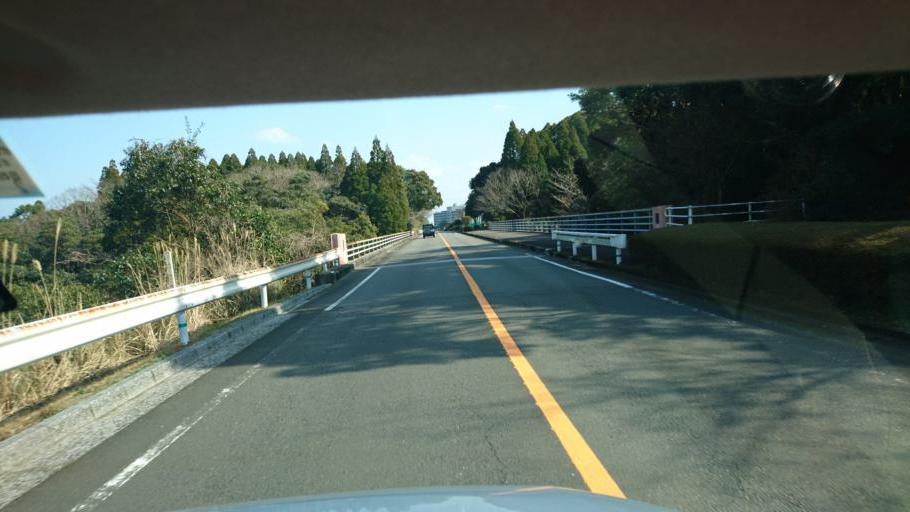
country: JP
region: Miyazaki
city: Miyazaki-shi
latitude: 31.8349
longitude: 131.4066
